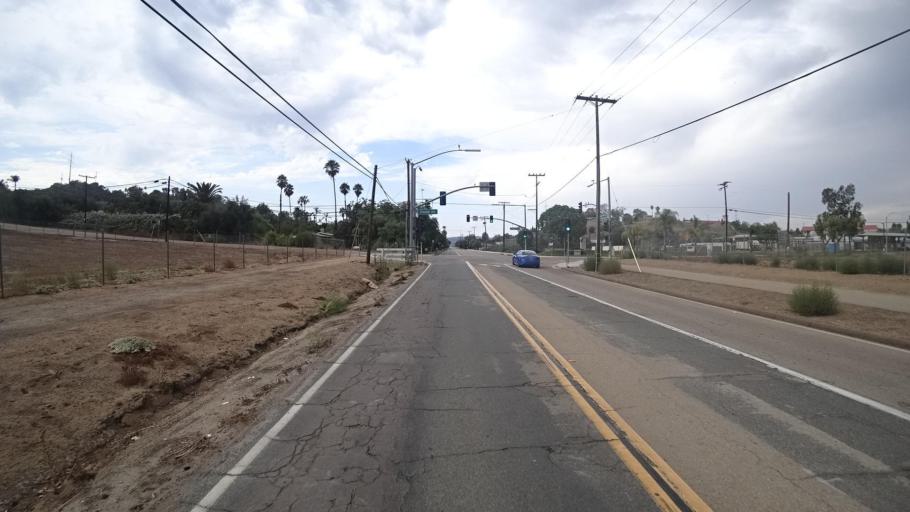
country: US
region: California
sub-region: San Diego County
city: Escondido
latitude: 33.1358
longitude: -117.1069
